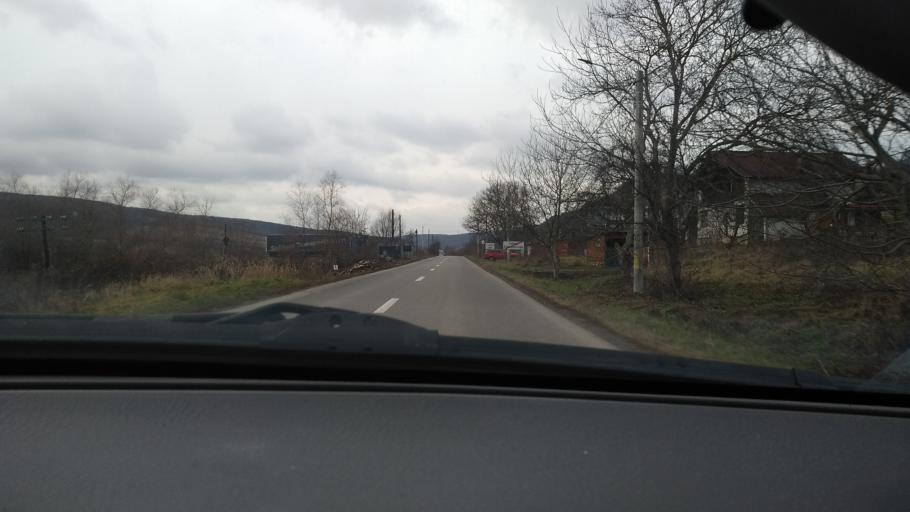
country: RO
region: Mures
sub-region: Comuna Livezeni
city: Livezeni
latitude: 46.5445
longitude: 24.6590
